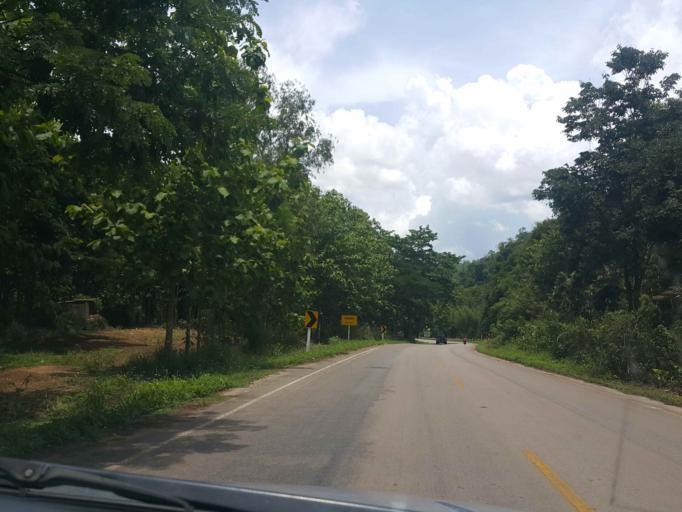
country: TH
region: Phayao
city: Chiang Muan
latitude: 18.8980
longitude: 100.1349
